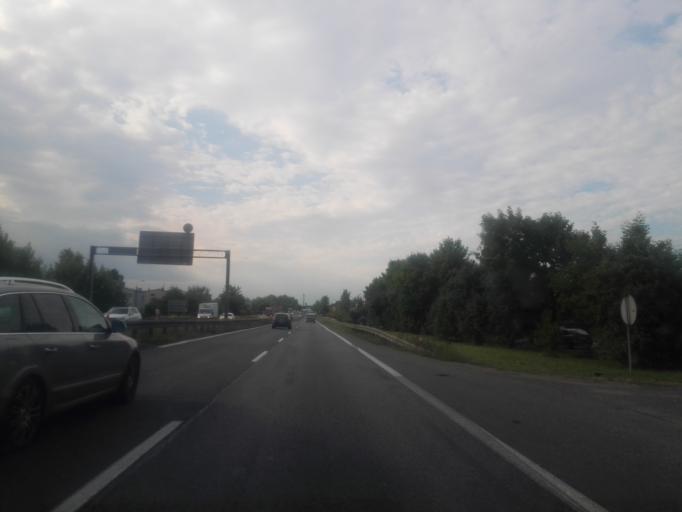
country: PL
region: Silesian Voivodeship
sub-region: Powiat bedzinski
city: Siewierz
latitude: 50.4685
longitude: 19.2298
